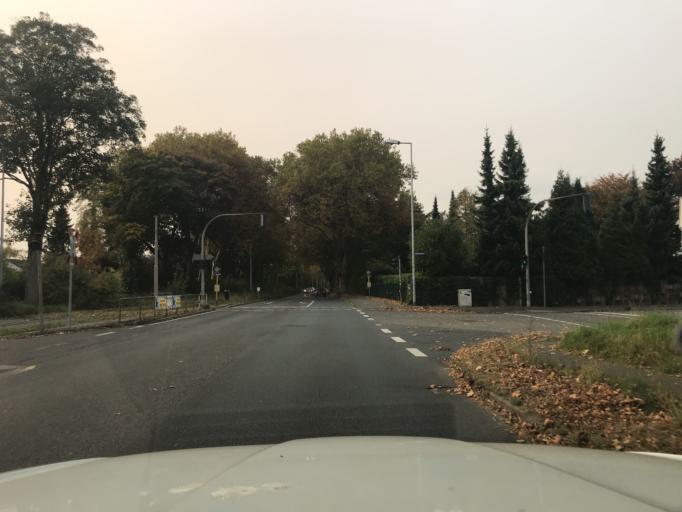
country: DE
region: North Rhine-Westphalia
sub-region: Regierungsbezirk Dusseldorf
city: Muelheim (Ruhr)
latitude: 51.4091
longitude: 6.9329
